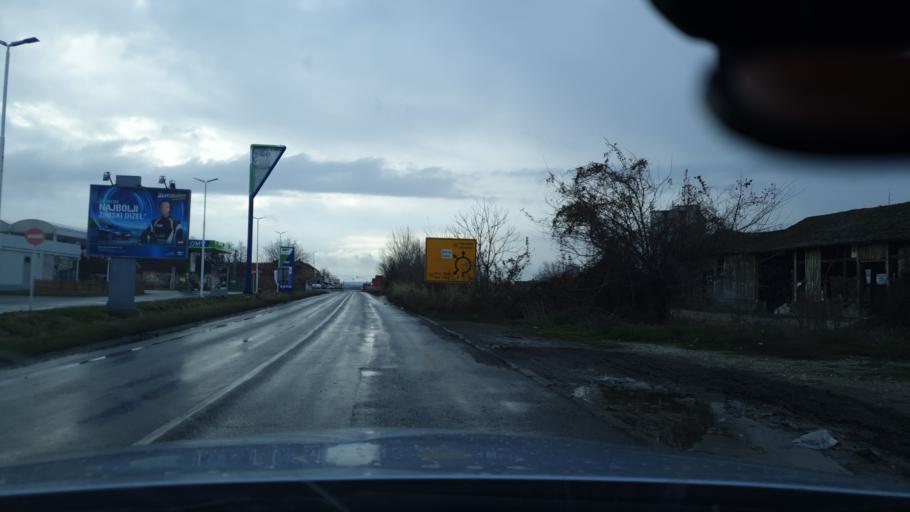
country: RS
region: Autonomna Pokrajina Vojvodina
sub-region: Juznobanatski Okrug
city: Kovin
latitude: 44.7516
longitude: 20.9666
